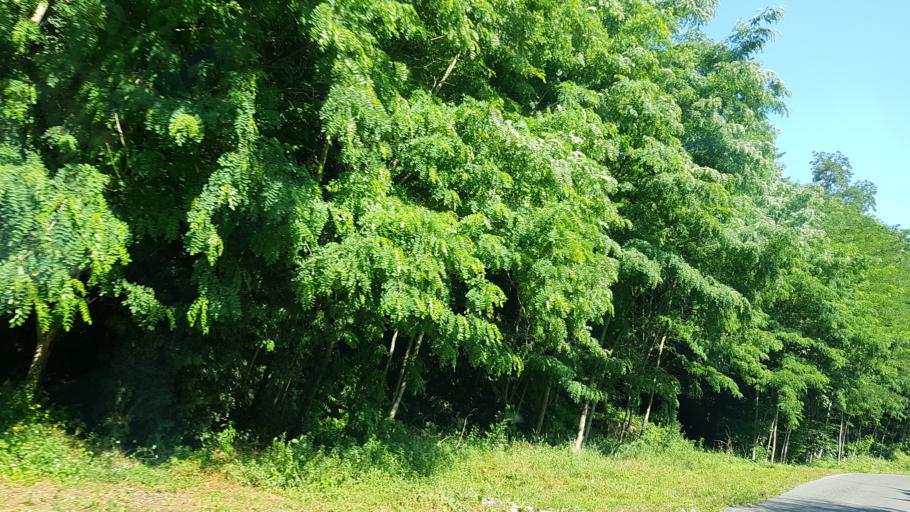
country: IT
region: Liguria
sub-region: Provincia di Genova
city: Serra Ricco
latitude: 44.5166
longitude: 8.9395
